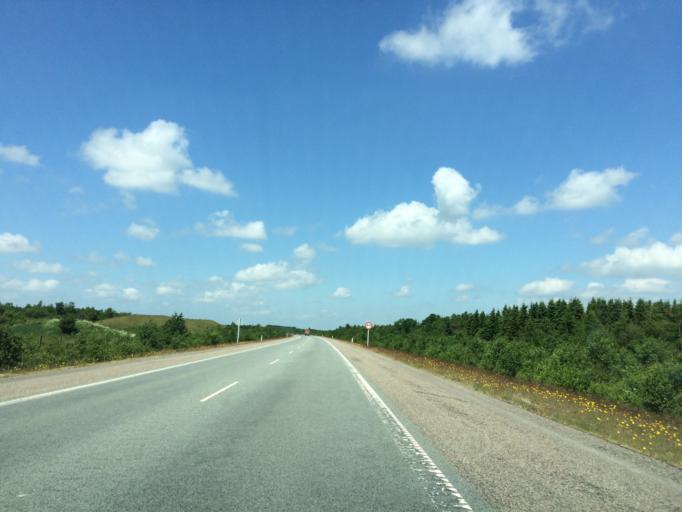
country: DK
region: Central Jutland
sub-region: Herning Kommune
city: Herning
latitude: 56.1705
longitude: 8.9951
